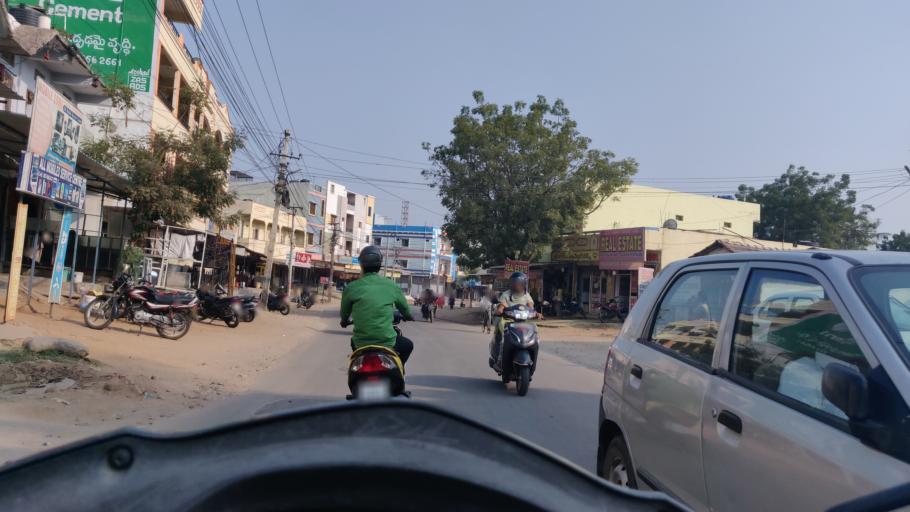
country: IN
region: Telangana
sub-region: Rangareddi
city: Uppal Kalan
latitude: 17.3950
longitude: 78.5935
